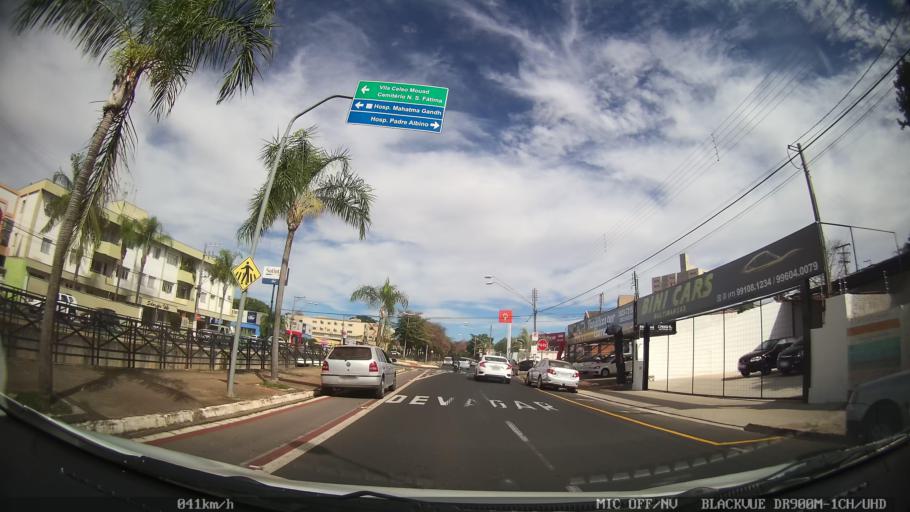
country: BR
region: Sao Paulo
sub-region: Catanduva
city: Catanduva
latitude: -21.1432
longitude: -48.9710
